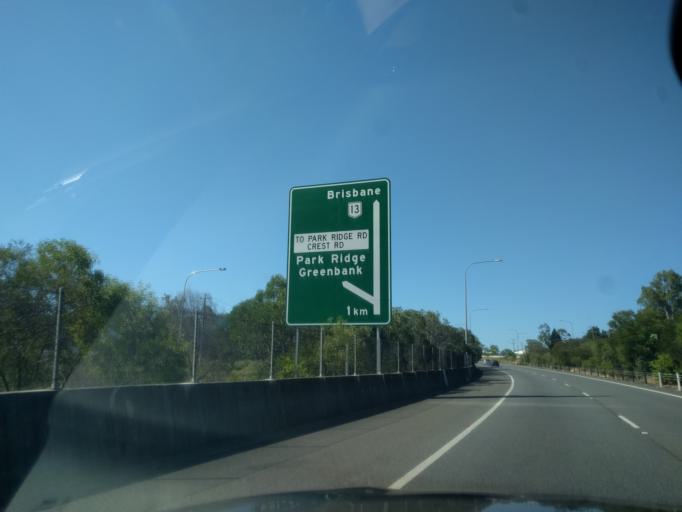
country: AU
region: Queensland
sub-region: Logan
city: Park Ridge South
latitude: -27.7111
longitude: 153.0371
